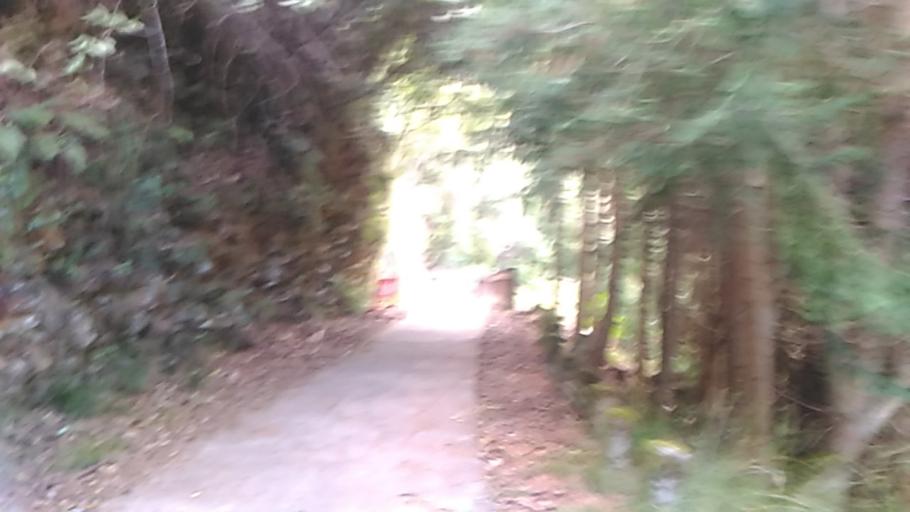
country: TW
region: Taiwan
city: Daxi
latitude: 24.4114
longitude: 121.3028
